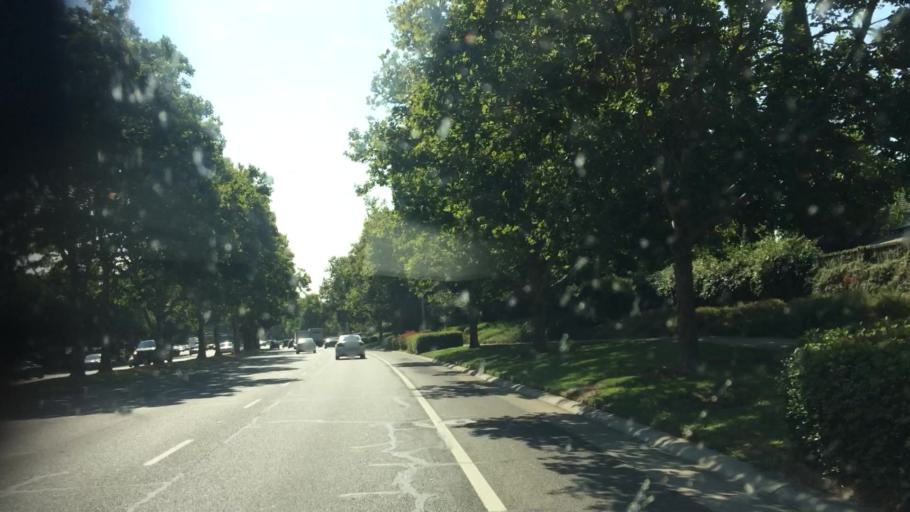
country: US
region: California
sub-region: Sacramento County
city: Laguna
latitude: 38.4223
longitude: -121.4107
